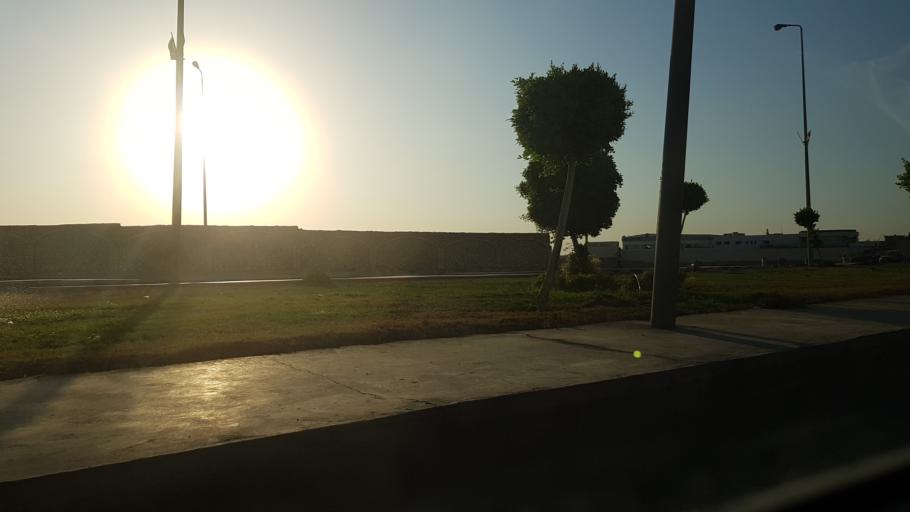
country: EG
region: Muhafazat al Qalyubiyah
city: Al Khankah
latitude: 30.0472
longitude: 31.4427
